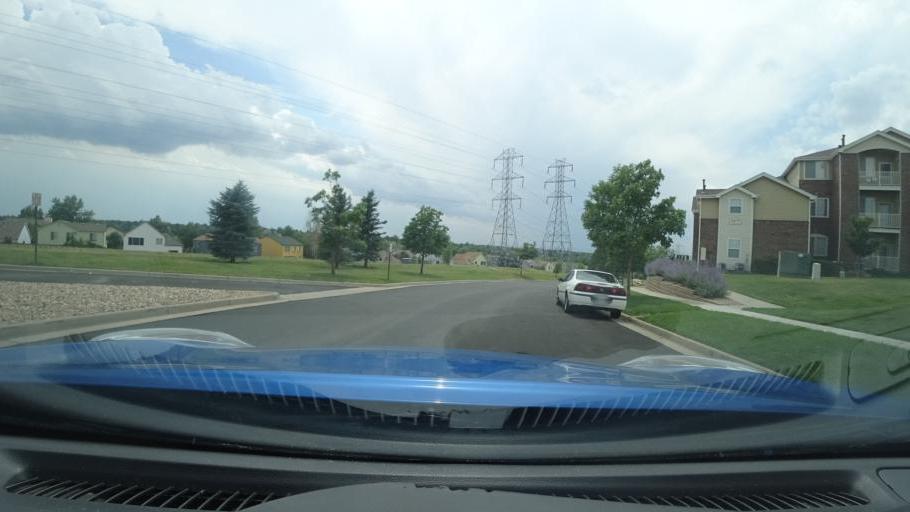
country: US
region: Colorado
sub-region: Adams County
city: Aurora
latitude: 39.6681
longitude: -104.7636
